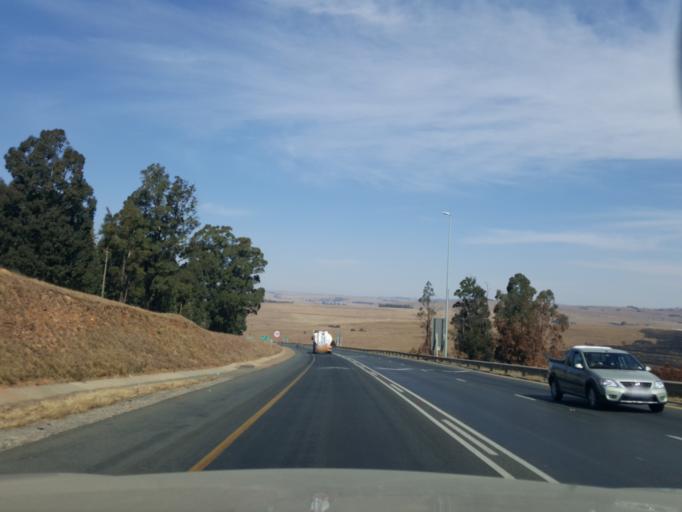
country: ZA
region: Mpumalanga
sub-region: Nkangala District Municipality
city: Belfast
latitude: -25.6315
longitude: 30.2556
